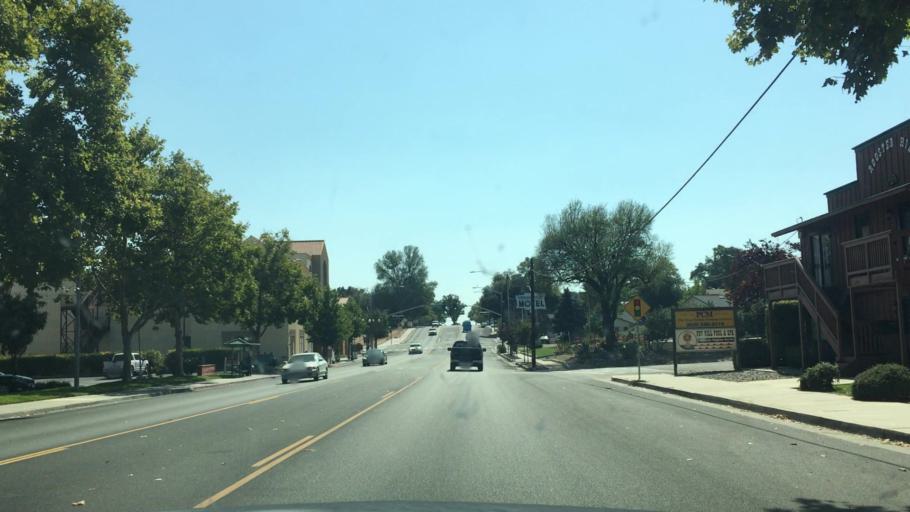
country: US
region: California
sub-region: San Luis Obispo County
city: Paso Robles
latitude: 35.6198
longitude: -120.6909
